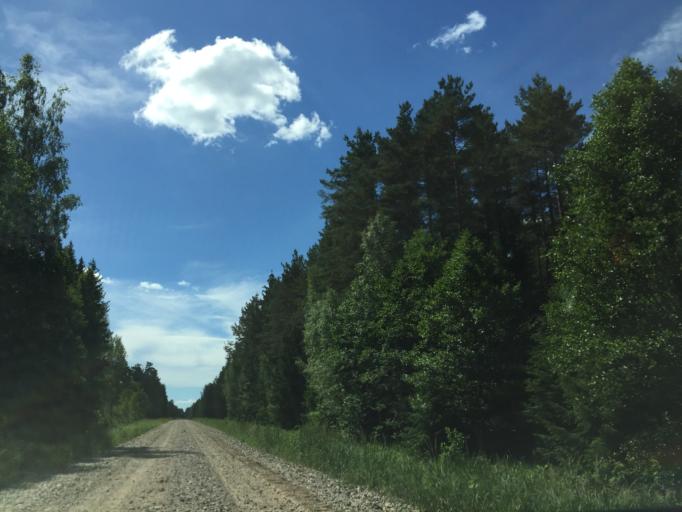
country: LV
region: Ventspils Rajons
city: Piltene
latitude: 57.2634
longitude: 21.8364
